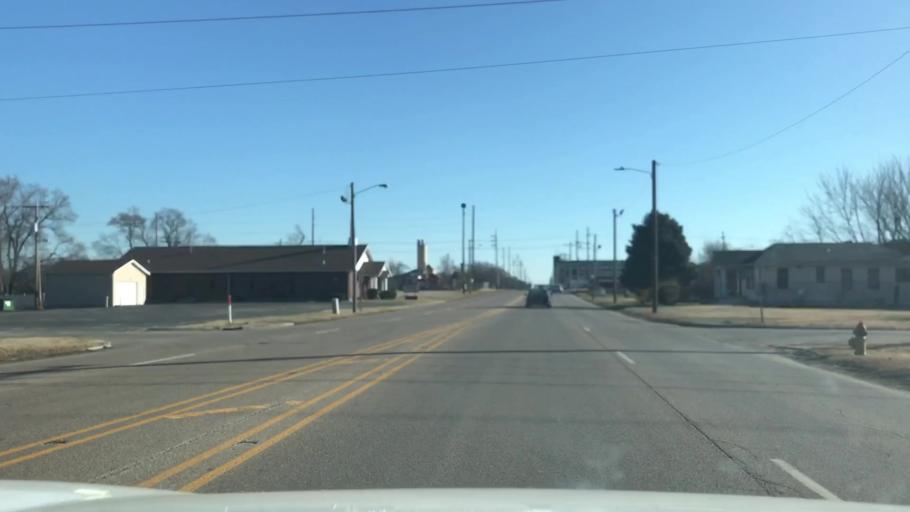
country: US
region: Illinois
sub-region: Saint Clair County
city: Alorton
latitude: 38.6047
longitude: -90.1335
